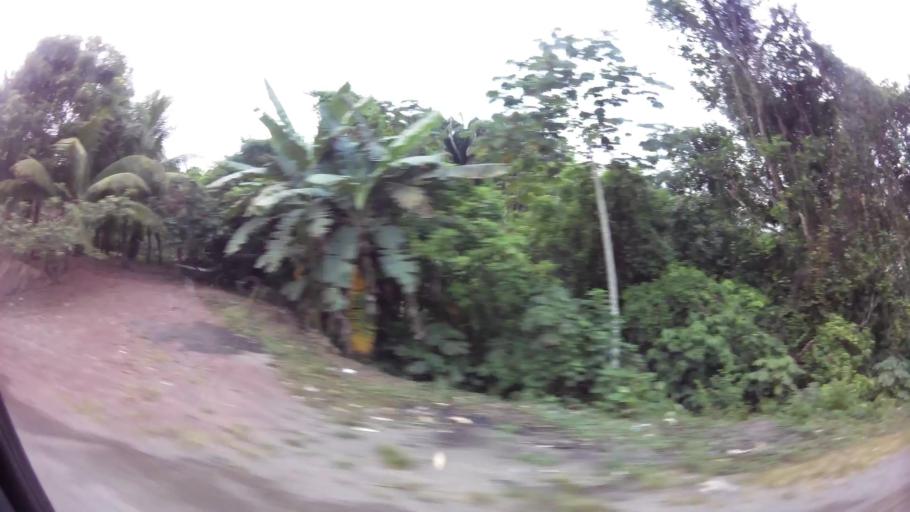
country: HN
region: Yoro
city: Guaimitas
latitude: 15.5051
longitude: -87.6961
